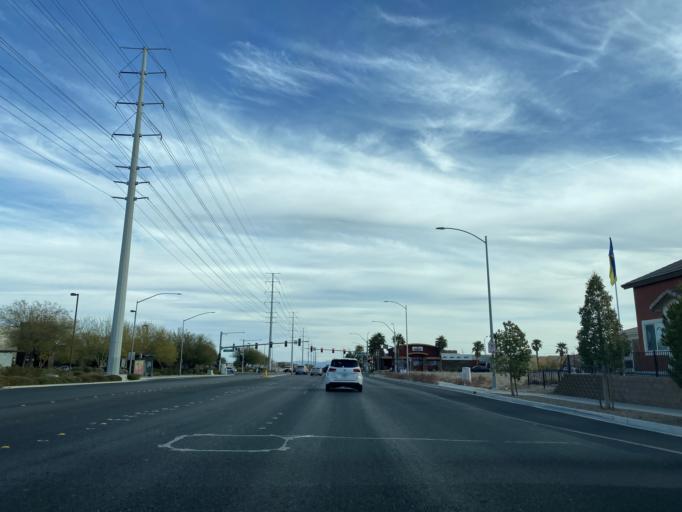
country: US
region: Nevada
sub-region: Clark County
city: Enterprise
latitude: 36.0556
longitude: -115.2536
